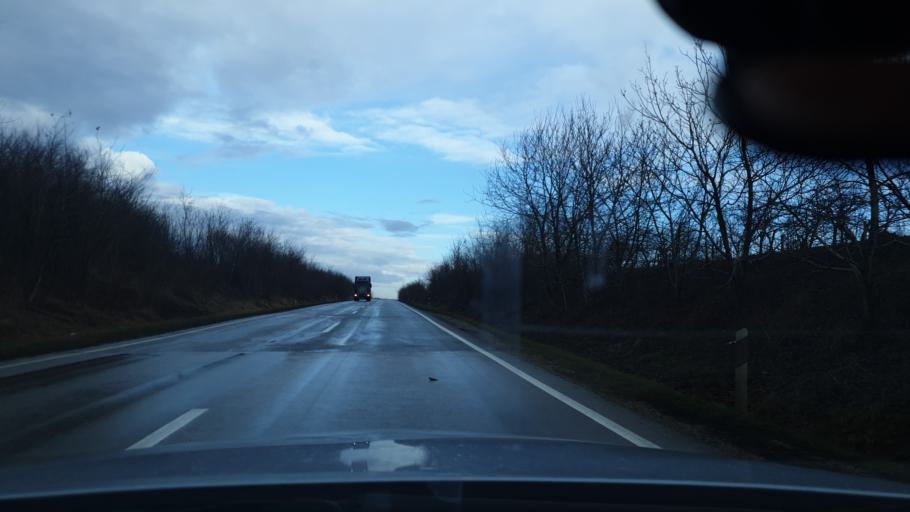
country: RS
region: Central Serbia
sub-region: Podunavski Okrug
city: Smederevo
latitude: 44.5982
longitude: 20.9559
